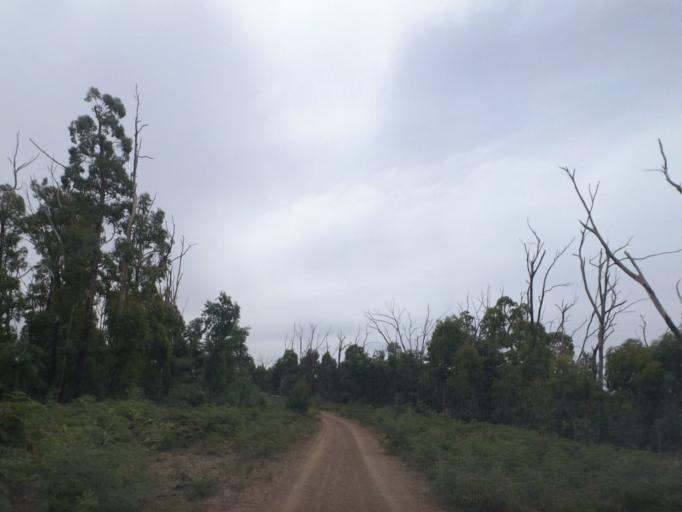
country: AU
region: Victoria
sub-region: Murrindindi
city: Alexandra
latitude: -37.3808
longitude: 145.5672
